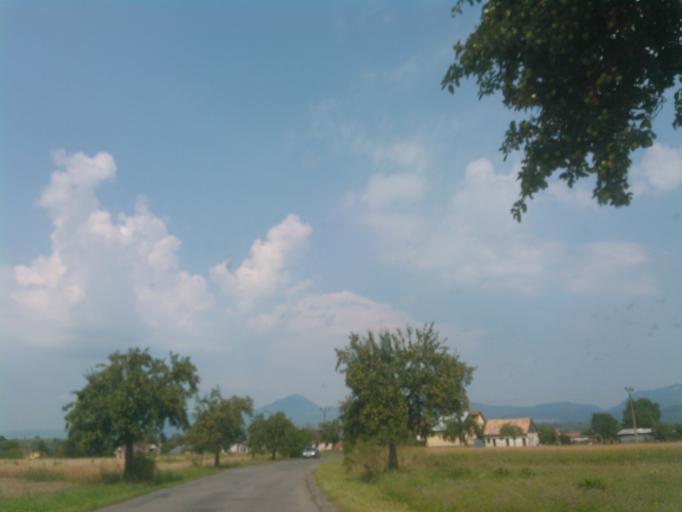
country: SK
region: Zilinsky
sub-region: Okres Liptovsky Mikulas
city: Liptovsky Mikulas
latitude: 49.0477
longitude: 19.4867
